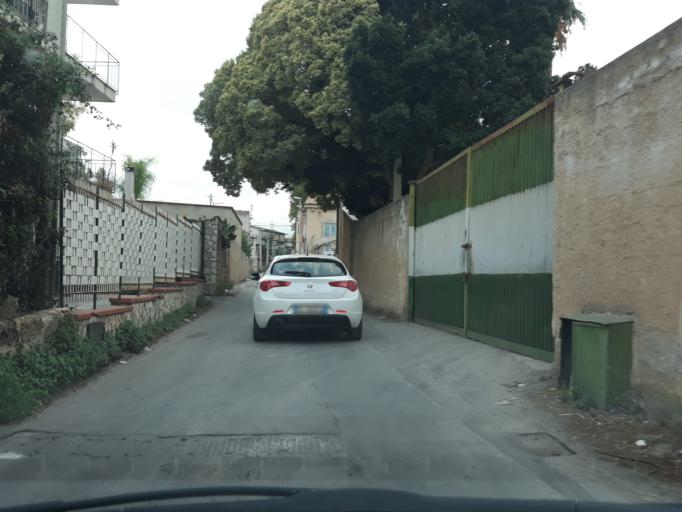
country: IT
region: Sicily
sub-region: Palermo
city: Monreale
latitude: 38.0925
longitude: 13.3162
